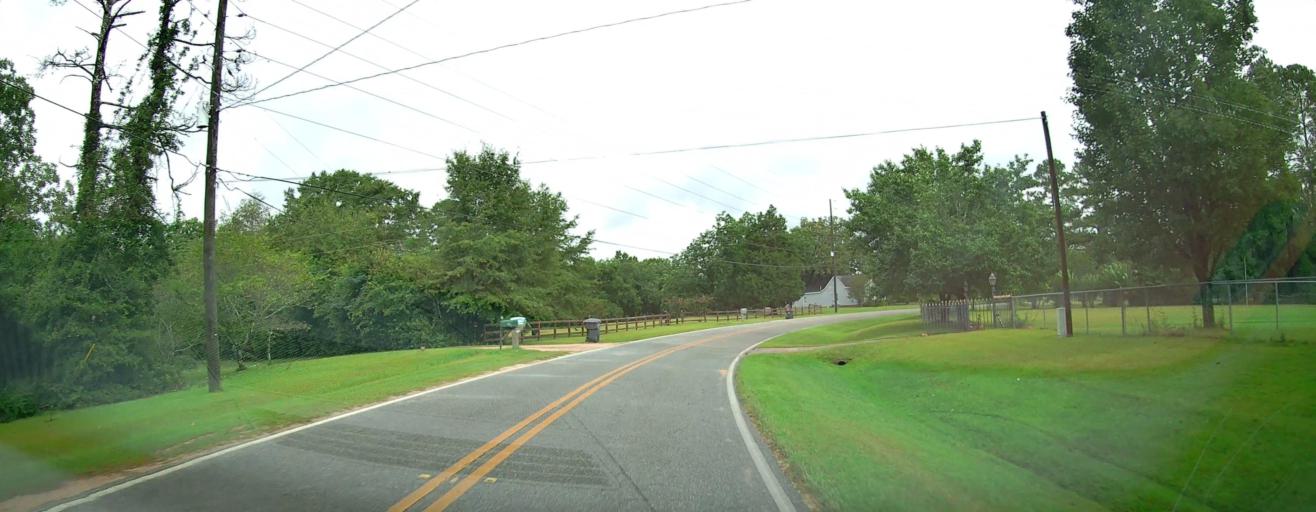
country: US
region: Georgia
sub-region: Bibb County
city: West Point
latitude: 32.7906
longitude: -83.8294
